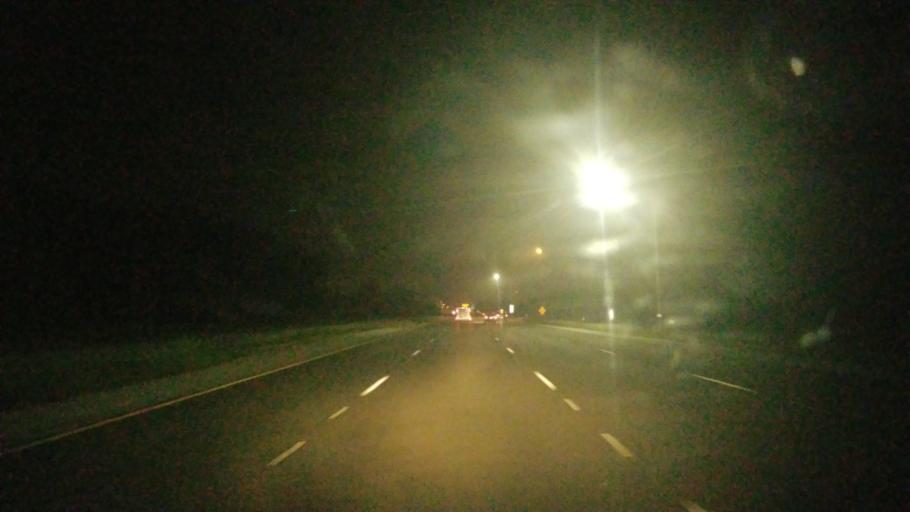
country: US
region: Illinois
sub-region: Madison County
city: Glen Carbon
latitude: 38.7568
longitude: -90.0159
